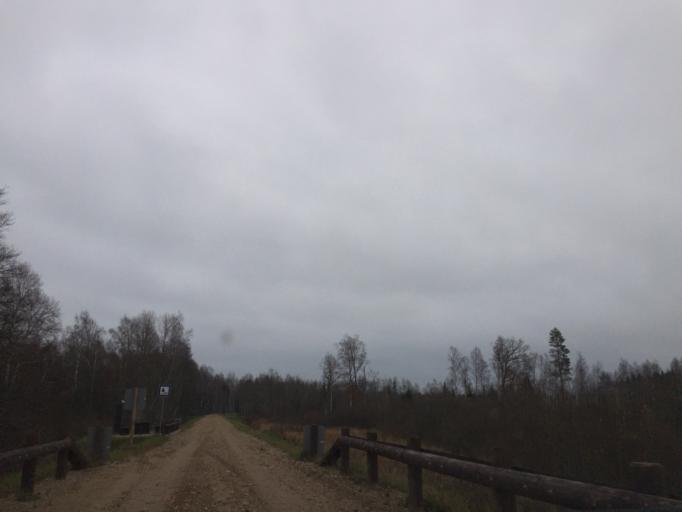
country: LV
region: Burtnieki
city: Matisi
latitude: 57.5468
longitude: 25.1485
